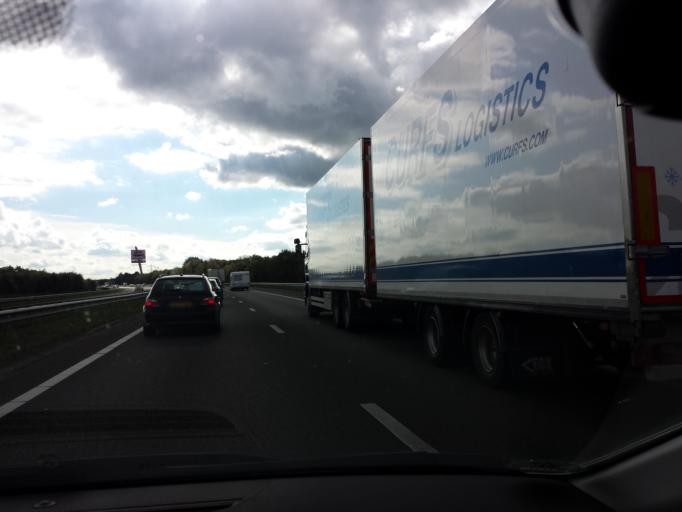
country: NL
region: Limburg
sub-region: Gemeente Venray
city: Venray
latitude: 51.5571
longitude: 5.9923
